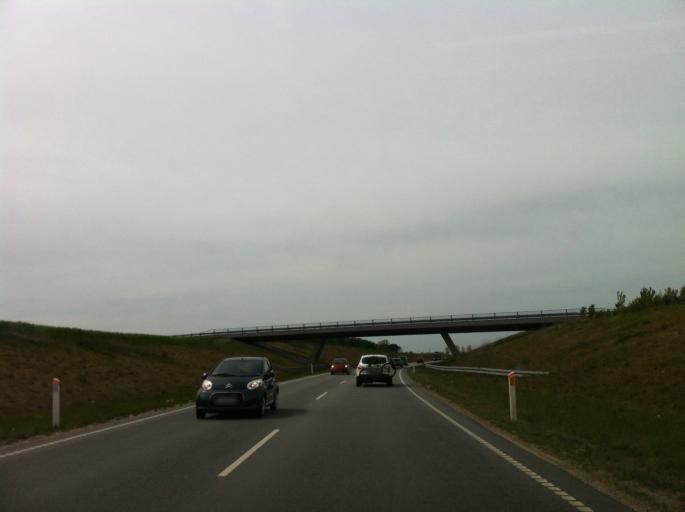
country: DK
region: Capital Region
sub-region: Frederikssund Kommune
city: Slangerup
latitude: 55.8809
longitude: 12.2039
